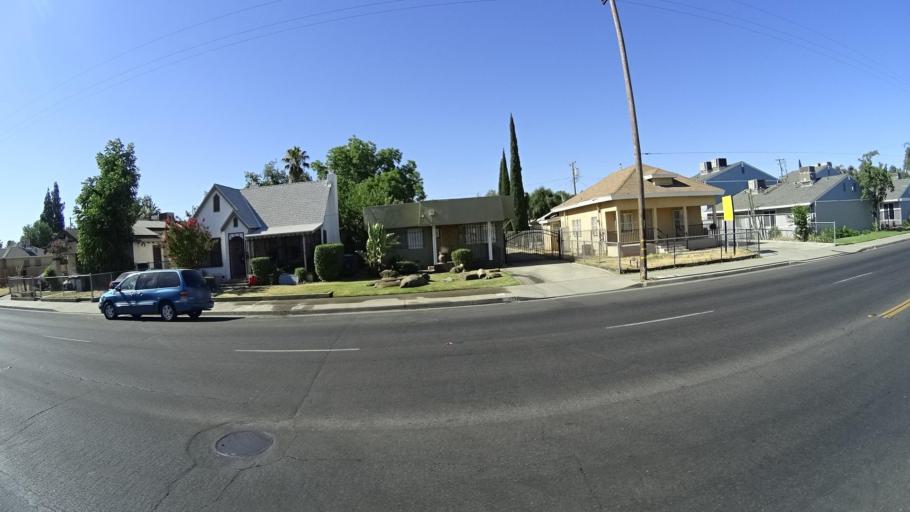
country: US
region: California
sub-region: Fresno County
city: Fresno
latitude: 36.7578
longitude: -119.7792
